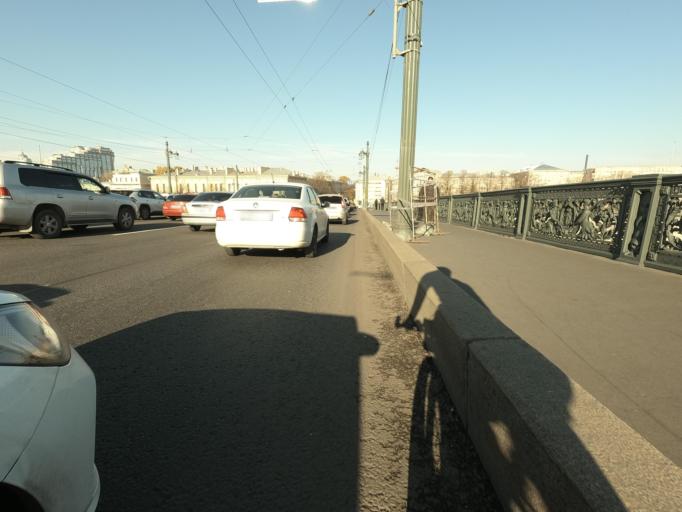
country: RU
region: Leningrad
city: Finlyandskiy
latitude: 59.9534
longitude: 30.3487
